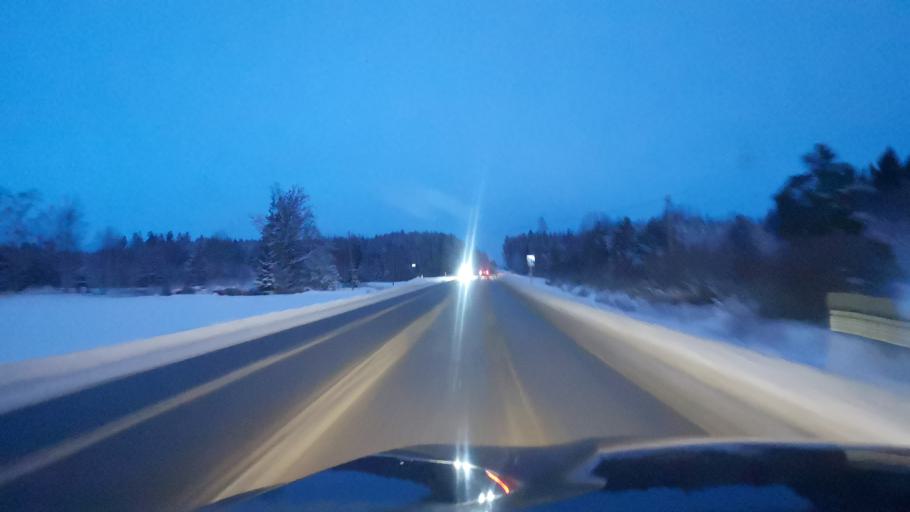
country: FI
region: Varsinais-Suomi
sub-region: Loimaa
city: Loimaa
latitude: 60.8664
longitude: 23.0544
